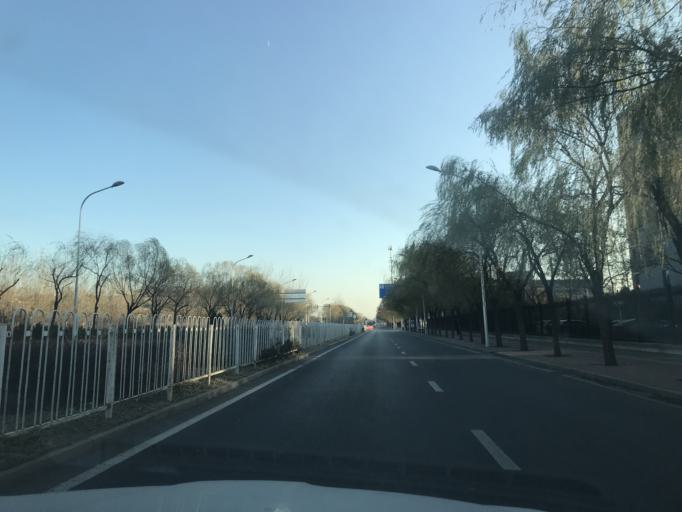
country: CN
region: Beijing
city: Xibeiwang
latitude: 40.0745
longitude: 116.2483
